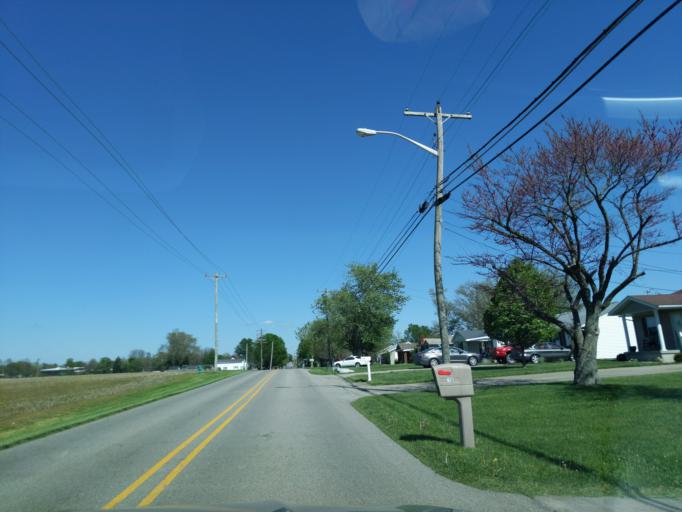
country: US
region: Indiana
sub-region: Decatur County
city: Greensburg
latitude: 39.3291
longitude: -85.4978
